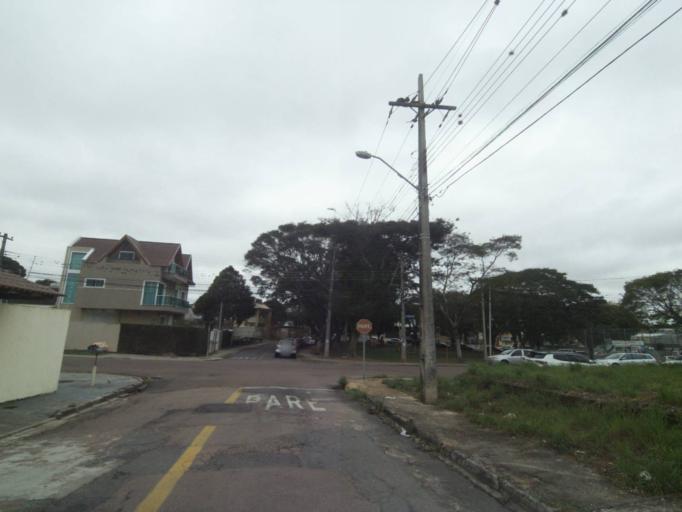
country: BR
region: Parana
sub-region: Curitiba
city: Curitiba
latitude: -25.4974
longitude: -49.2802
